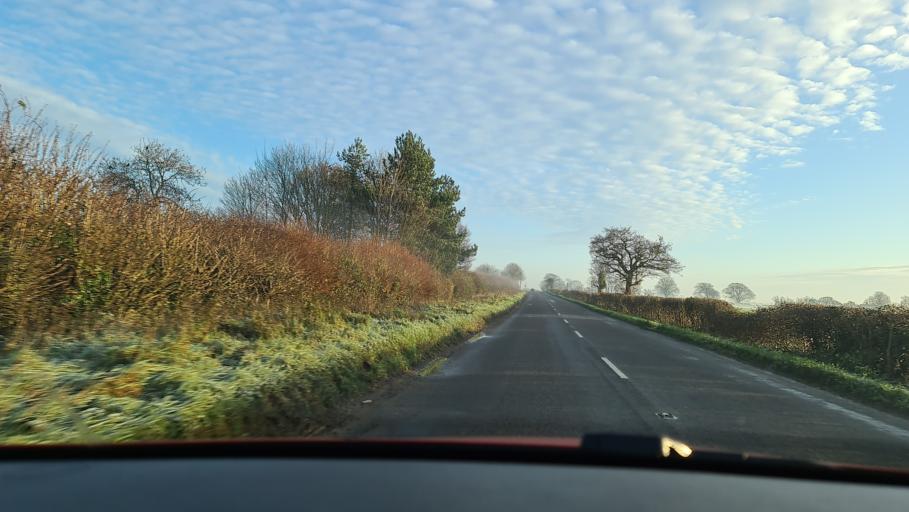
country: GB
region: England
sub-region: Buckinghamshire
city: Haddenham
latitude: 51.8070
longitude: -0.9512
